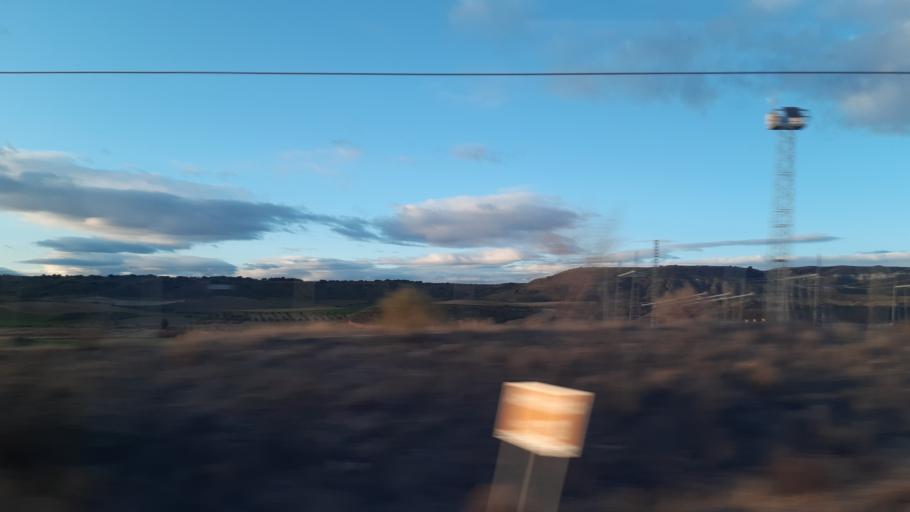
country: ES
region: Madrid
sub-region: Provincia de Madrid
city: Anchuelo
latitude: 40.4628
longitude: -3.2969
